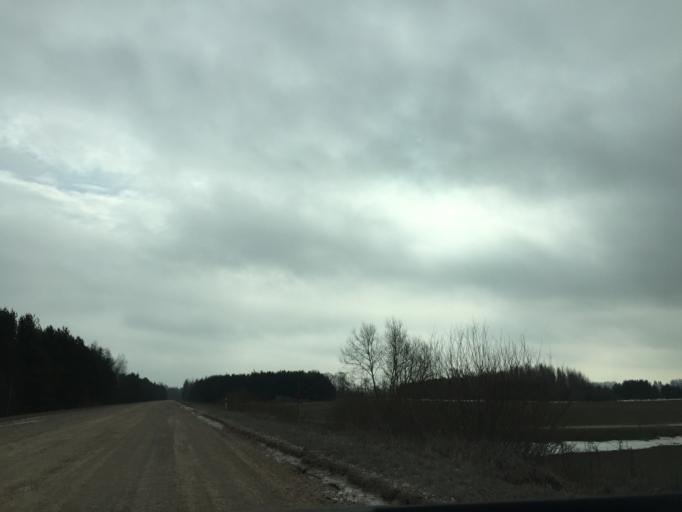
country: LV
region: Rundales
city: Pilsrundale
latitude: 56.5458
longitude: 23.9897
